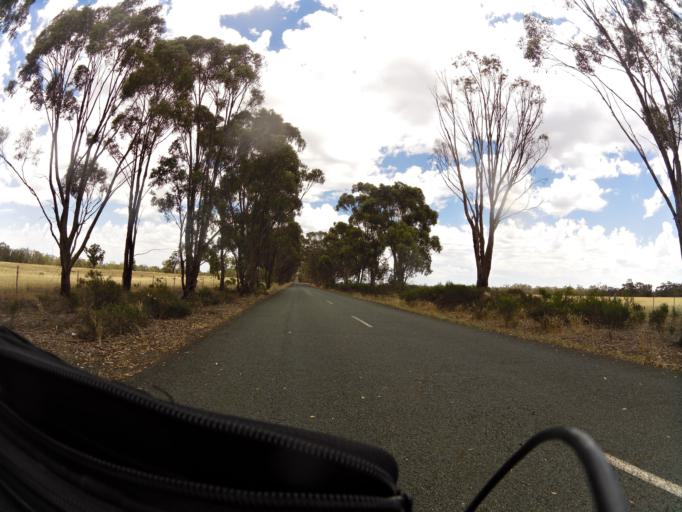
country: AU
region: Victoria
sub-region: Greater Shepparton
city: Shepparton
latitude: -36.6795
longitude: 145.1955
